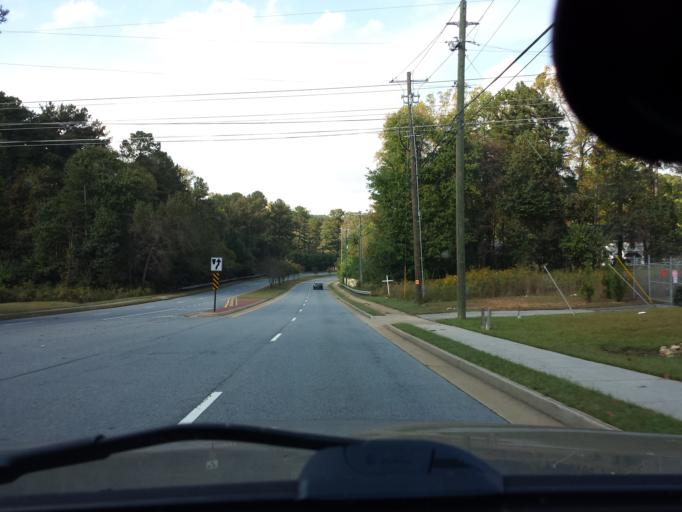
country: US
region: Georgia
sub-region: Cobb County
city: Marietta
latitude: 33.9900
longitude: -84.4888
